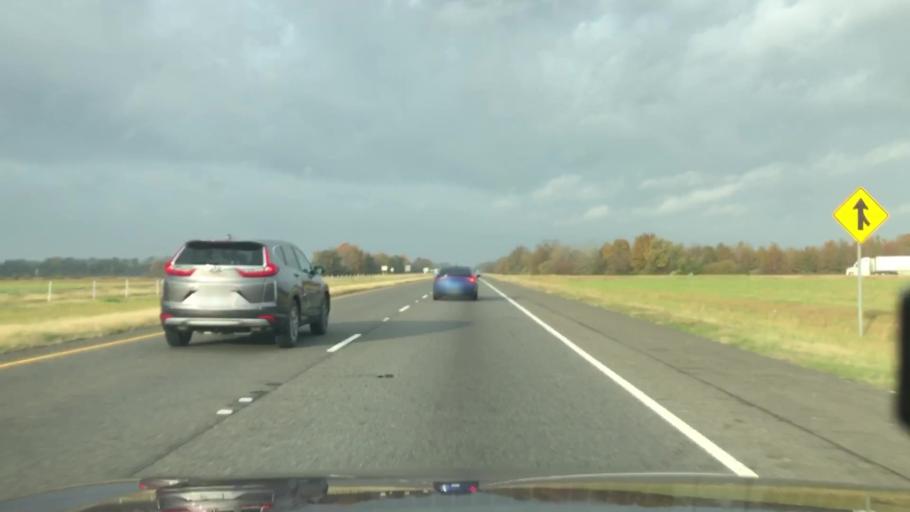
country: US
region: Louisiana
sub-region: Richland Parish
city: Delhi
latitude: 32.4316
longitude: -91.4195
